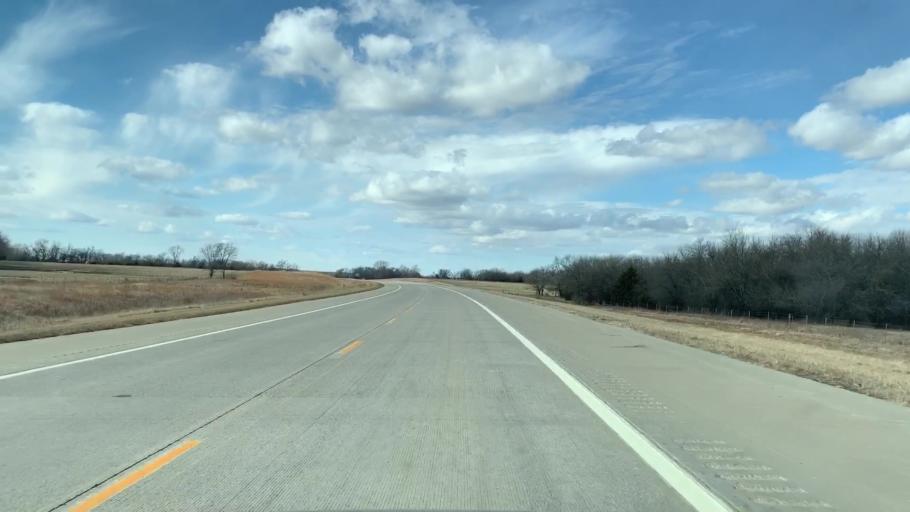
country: US
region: Kansas
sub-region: Labette County
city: Parsons
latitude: 37.3587
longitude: -95.2196
